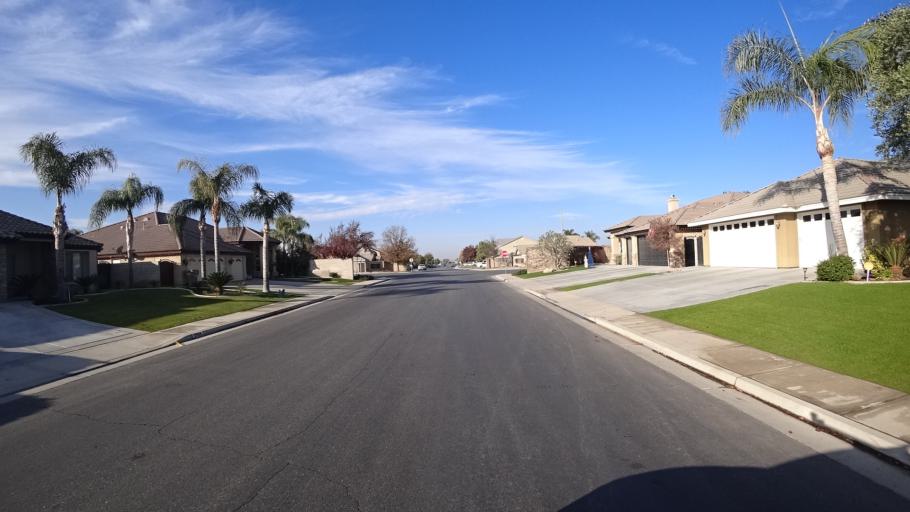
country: US
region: California
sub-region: Kern County
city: Rosedale
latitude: 35.4093
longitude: -119.1360
